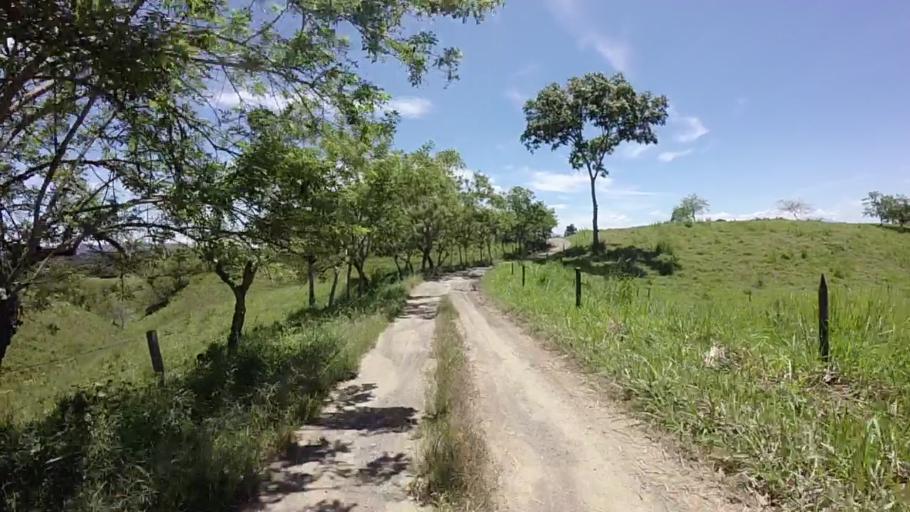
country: CO
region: Valle del Cauca
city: Alcala
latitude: 4.7103
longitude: -75.8090
